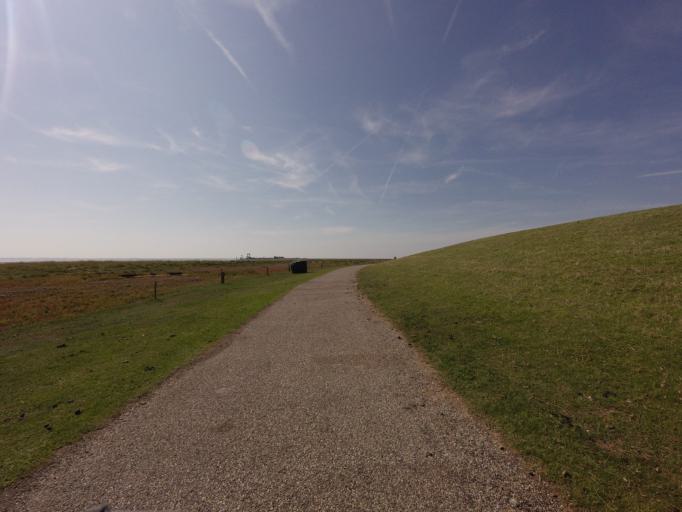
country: NL
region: Friesland
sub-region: Gemeente Schiermonnikoog
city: Schiermonnikoog
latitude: 53.4758
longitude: 6.2095
